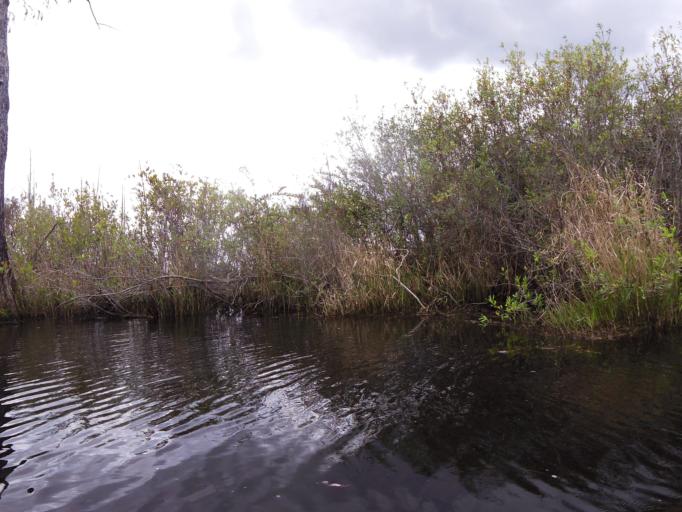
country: US
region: Georgia
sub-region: Charlton County
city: Folkston
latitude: 30.7359
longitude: -82.1619
